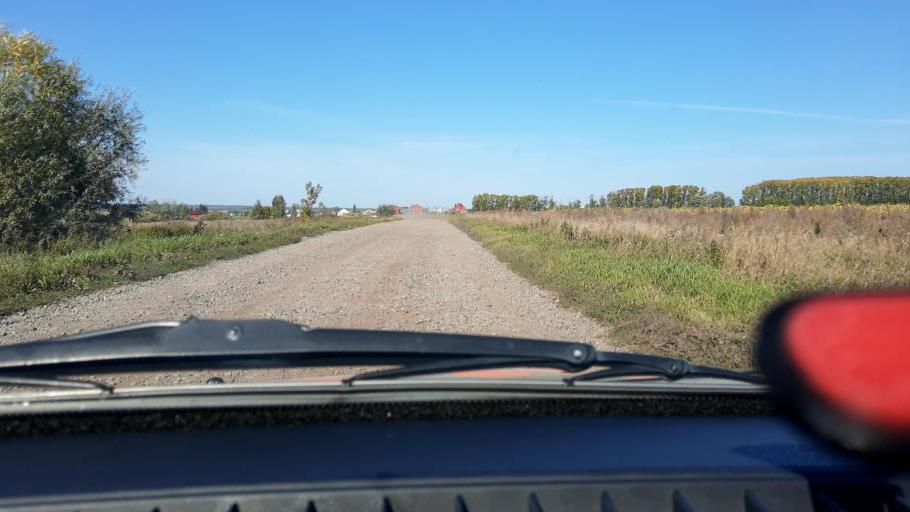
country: RU
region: Bashkortostan
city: Asanovo
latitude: 54.8088
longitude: 55.5851
